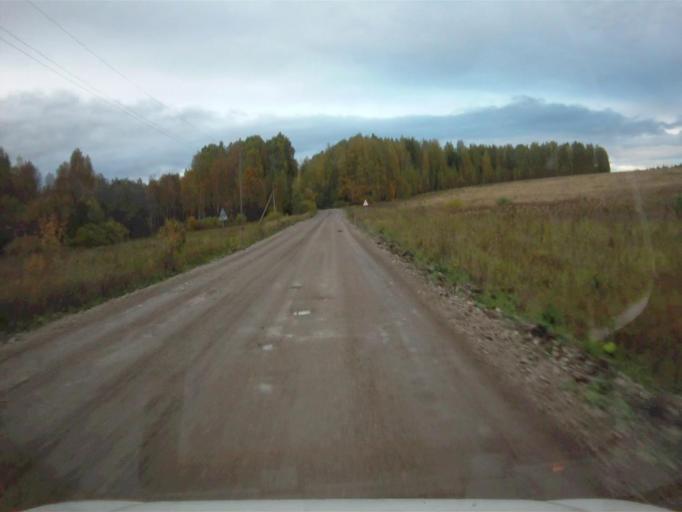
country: RU
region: Sverdlovsk
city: Mikhaylovsk
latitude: 56.1917
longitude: 59.1912
